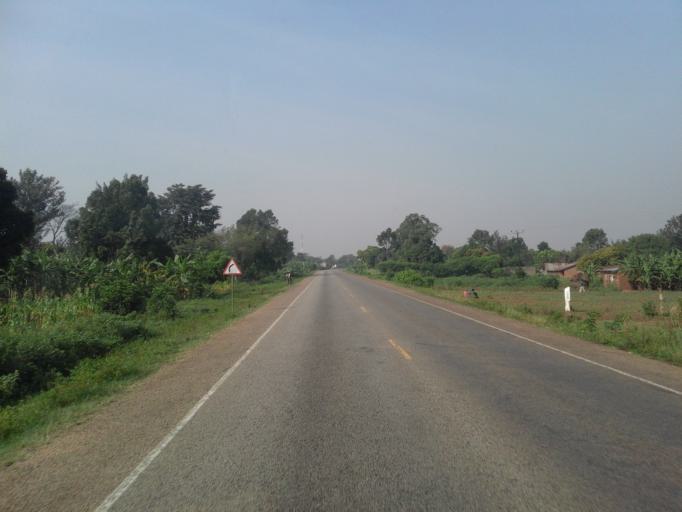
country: UG
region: Eastern Region
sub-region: Budaka District
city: Budaka
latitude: 1.0244
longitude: 33.9758
